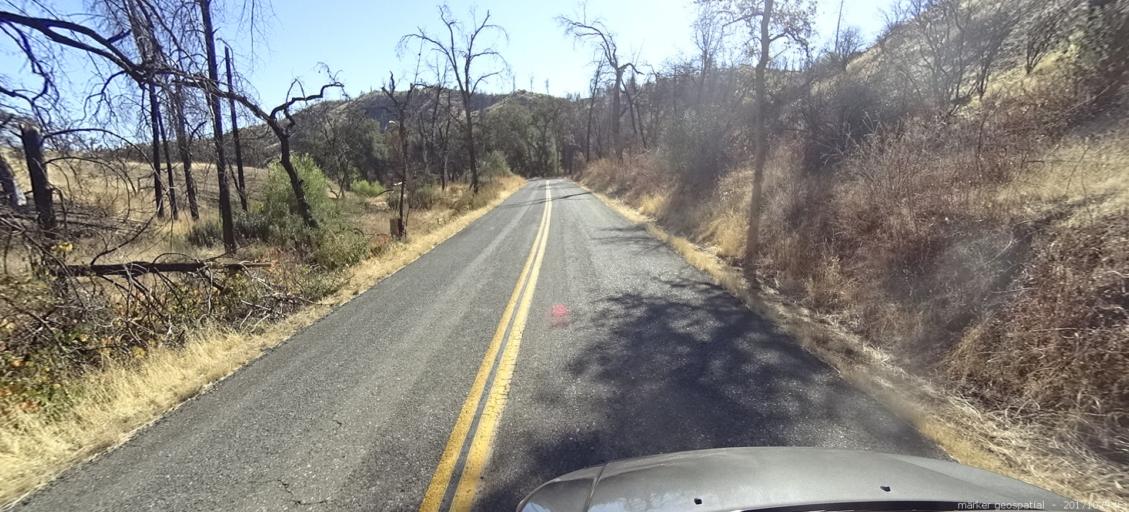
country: US
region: California
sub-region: Trinity County
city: Lewiston
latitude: 40.4203
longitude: -122.7498
